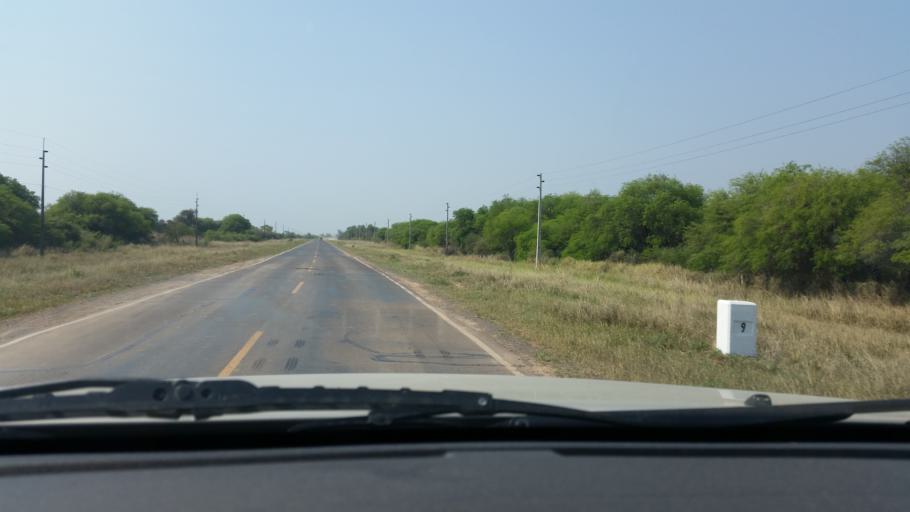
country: PY
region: Boqueron
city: Filadelfia
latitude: -22.4187
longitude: -60.0307
